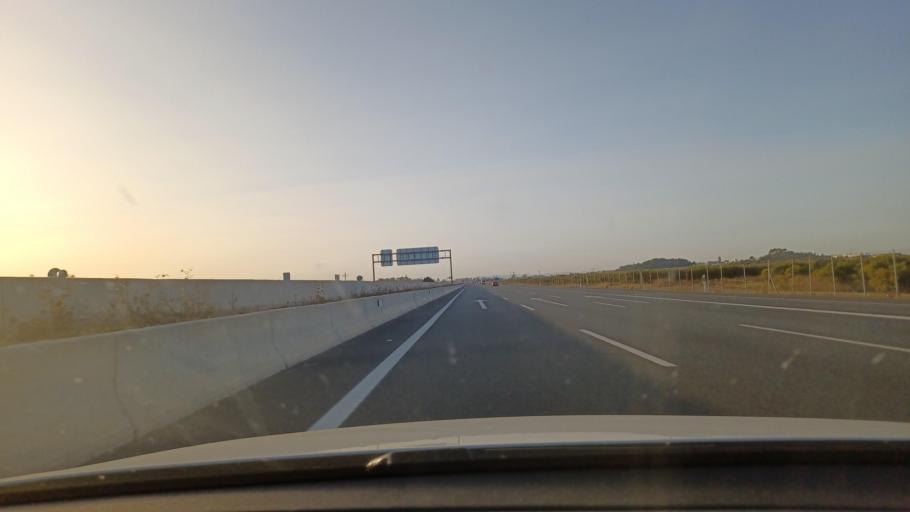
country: ES
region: Valencia
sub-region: Provincia de Valencia
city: Pucol
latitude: 39.6116
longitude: -0.2944
